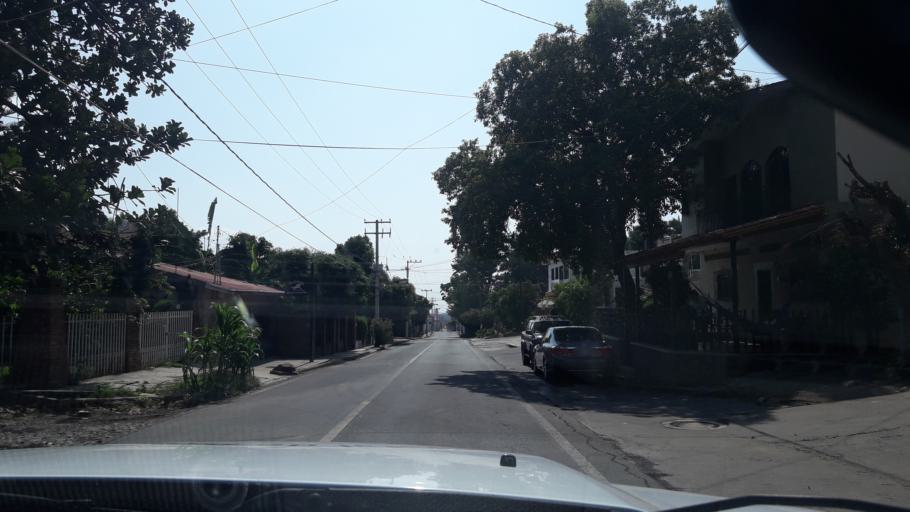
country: MX
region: Colima
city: Comala
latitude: 19.3308
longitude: -103.7535
